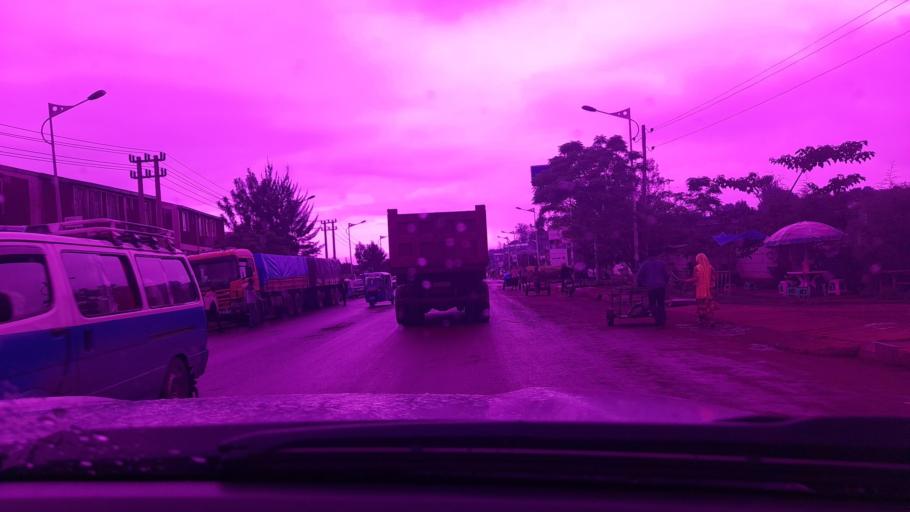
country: ET
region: Oromiya
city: Jima
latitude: 7.6682
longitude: 36.8460
